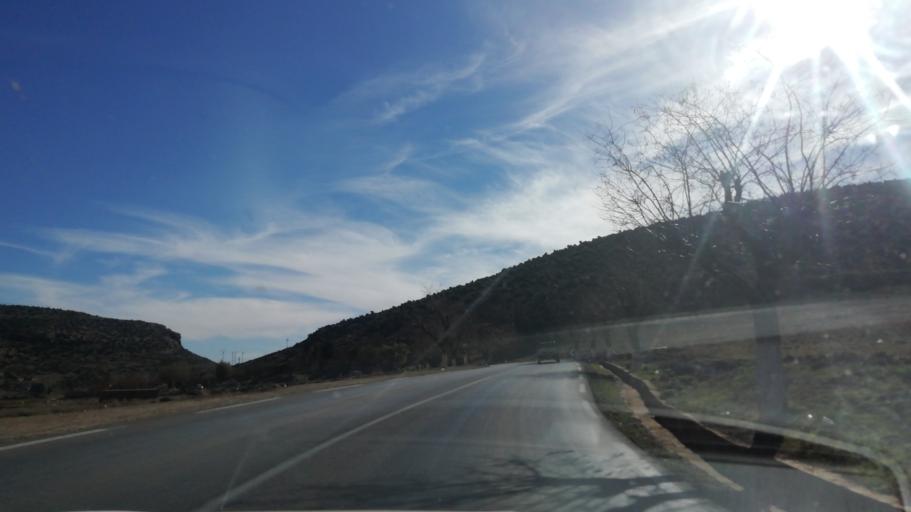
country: DZ
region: Tlemcen
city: Sebdou
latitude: 34.7008
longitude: -1.3153
